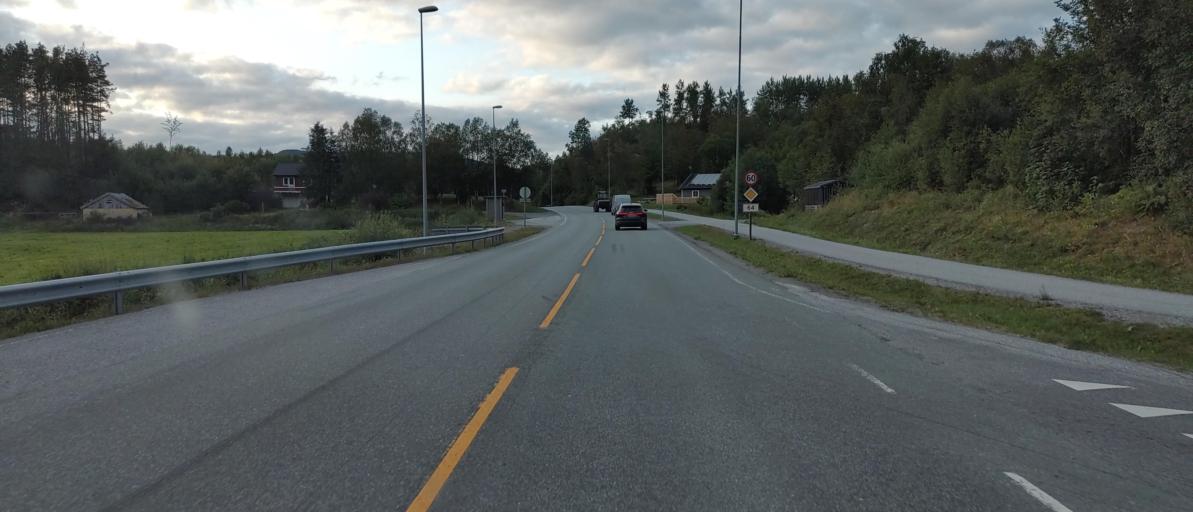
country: NO
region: More og Romsdal
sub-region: Molde
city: Molde
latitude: 62.7923
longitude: 7.2322
